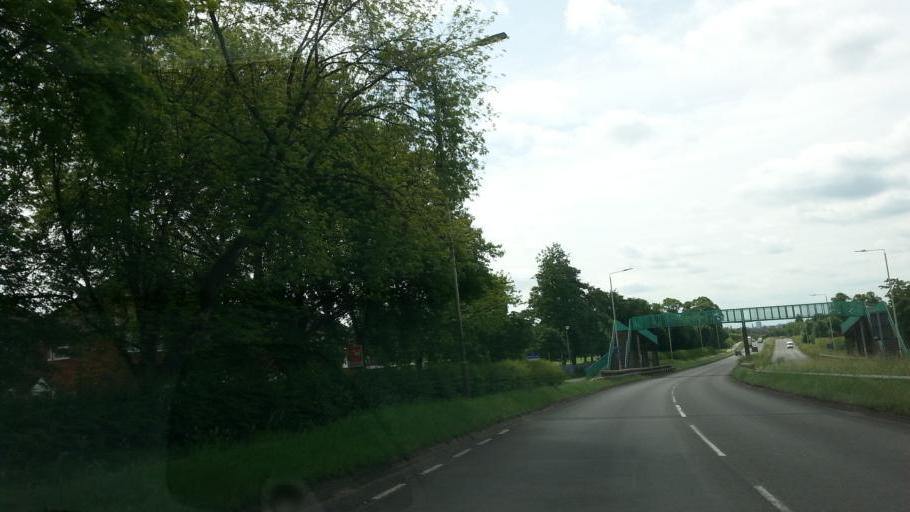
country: GB
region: England
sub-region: Leicestershire
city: Syston
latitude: 52.6812
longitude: -1.0928
